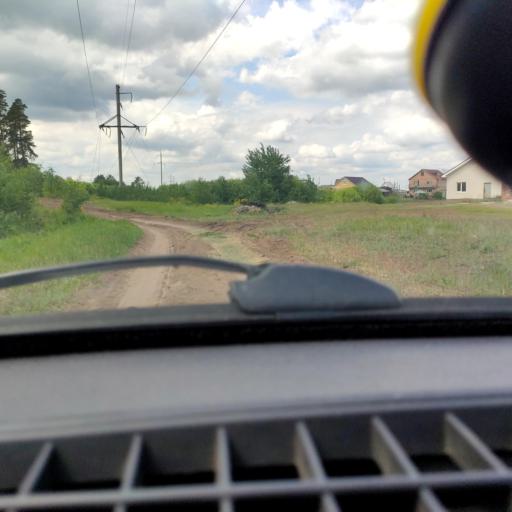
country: RU
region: Samara
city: Povolzhskiy
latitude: 53.6315
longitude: 49.6702
